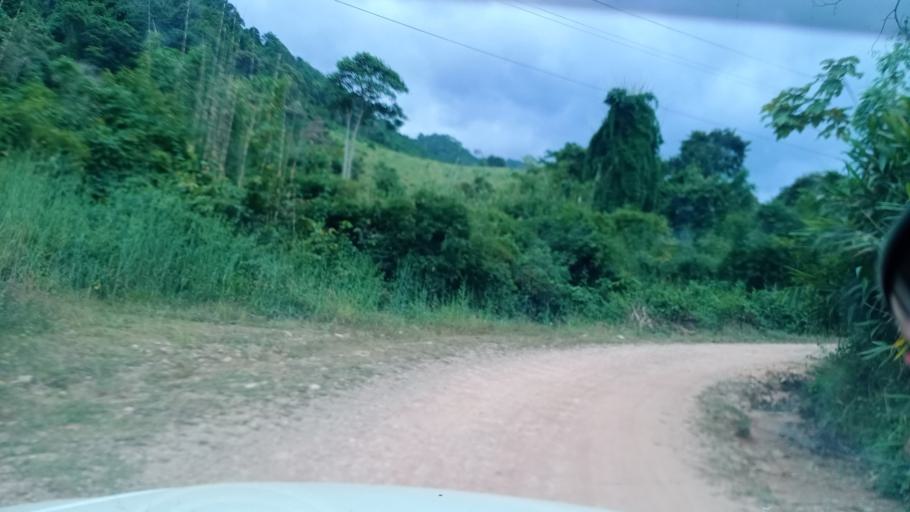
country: TH
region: Changwat Bueng Kan
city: Pak Khat
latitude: 18.7257
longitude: 103.2562
